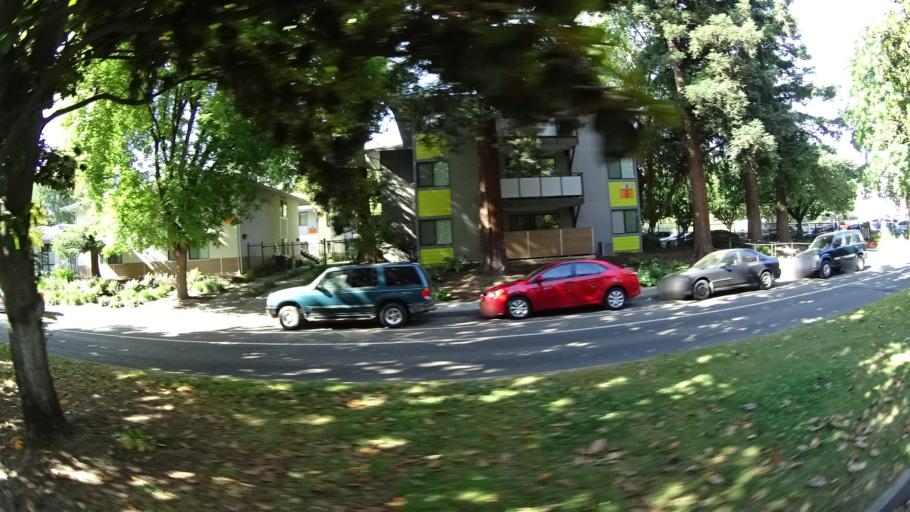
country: US
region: California
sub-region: Sacramento County
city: Rosemont
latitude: 38.5618
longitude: -121.4150
